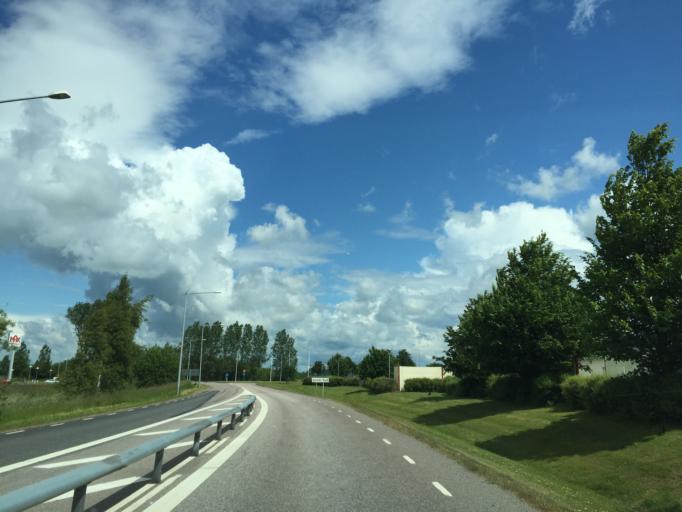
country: SE
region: Skane
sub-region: Kavlinge Kommun
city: Hofterup
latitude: 55.7698
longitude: 12.9875
